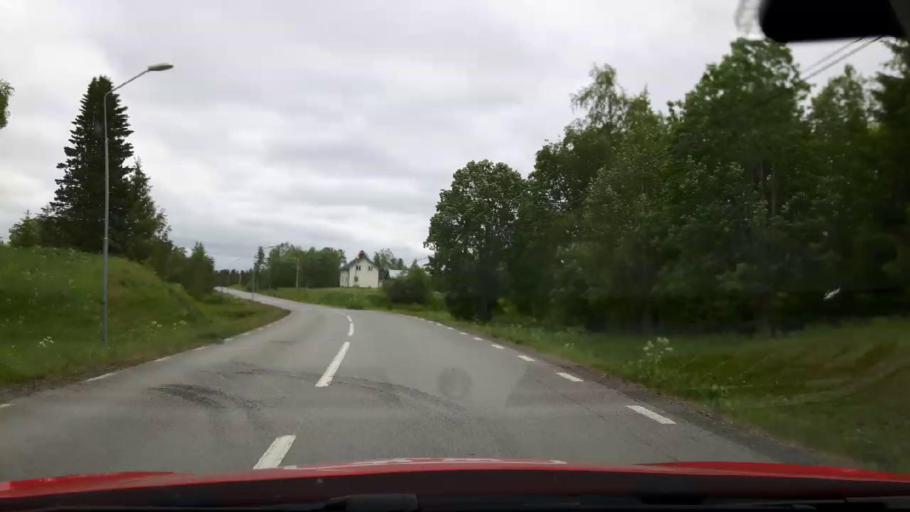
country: SE
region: Jaemtland
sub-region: OEstersunds Kommun
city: Lit
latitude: 63.6754
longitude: 15.0564
